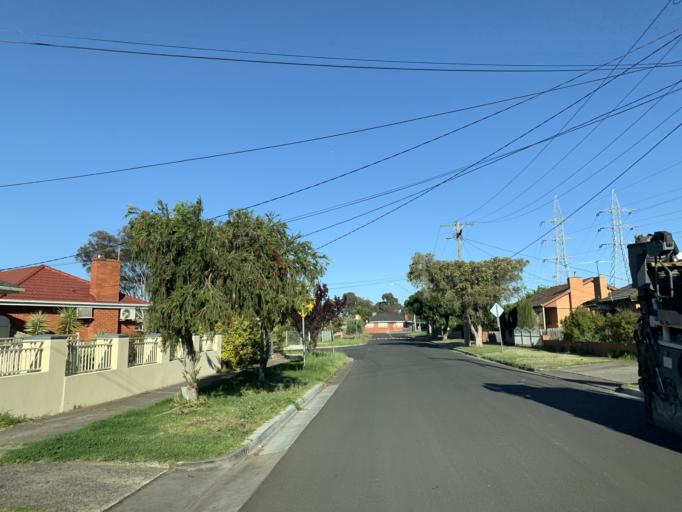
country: AU
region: Victoria
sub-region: Brimbank
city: St Albans
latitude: -37.7508
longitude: 144.8031
